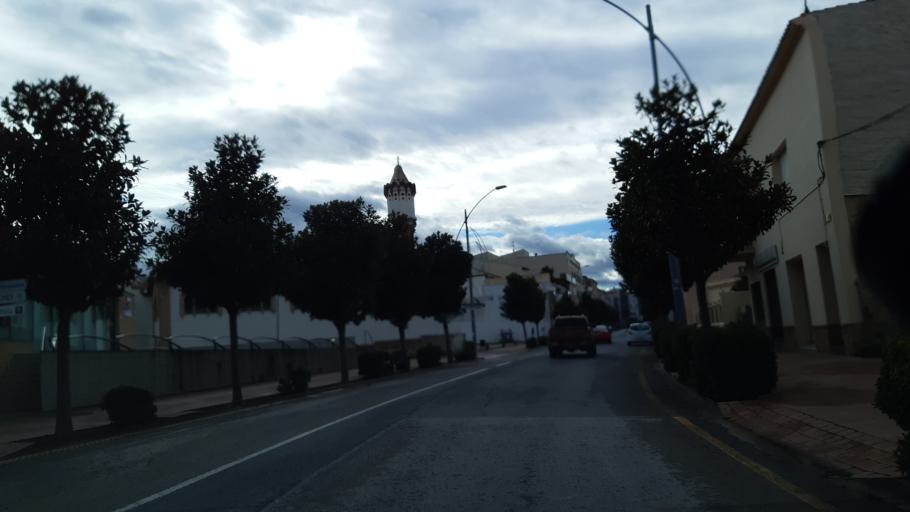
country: ES
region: Catalonia
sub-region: Provincia de Tarragona
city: Gandesa
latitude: 41.0556
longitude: 0.4406
